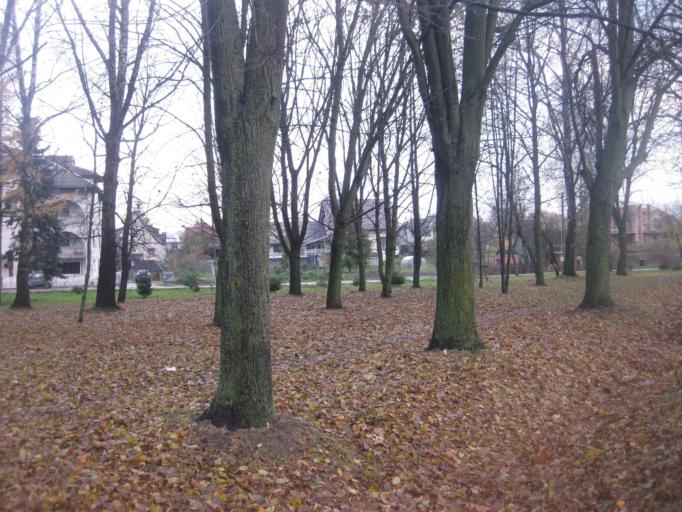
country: LT
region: Kauno apskritis
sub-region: Kaunas
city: Aleksotas
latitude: 54.8582
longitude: 23.8822
